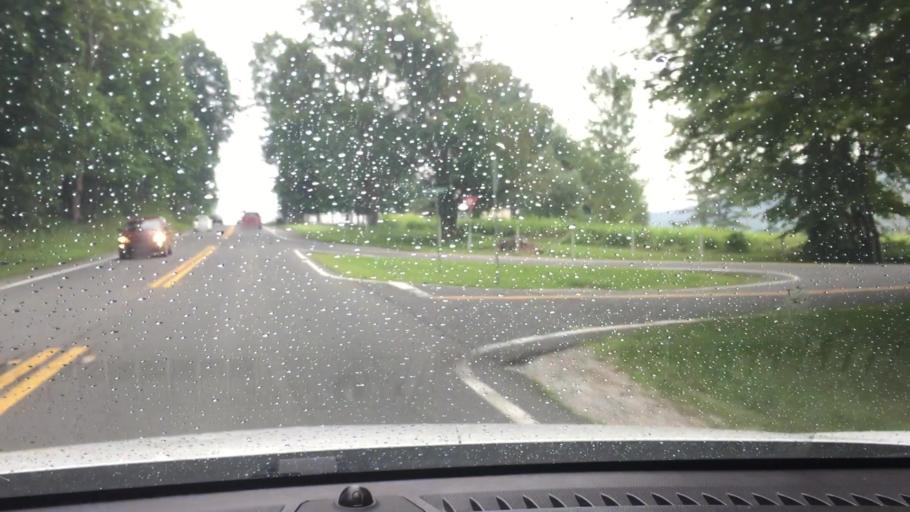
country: US
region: Massachusetts
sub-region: Berkshire County
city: Lenox
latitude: 42.3263
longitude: -73.2881
